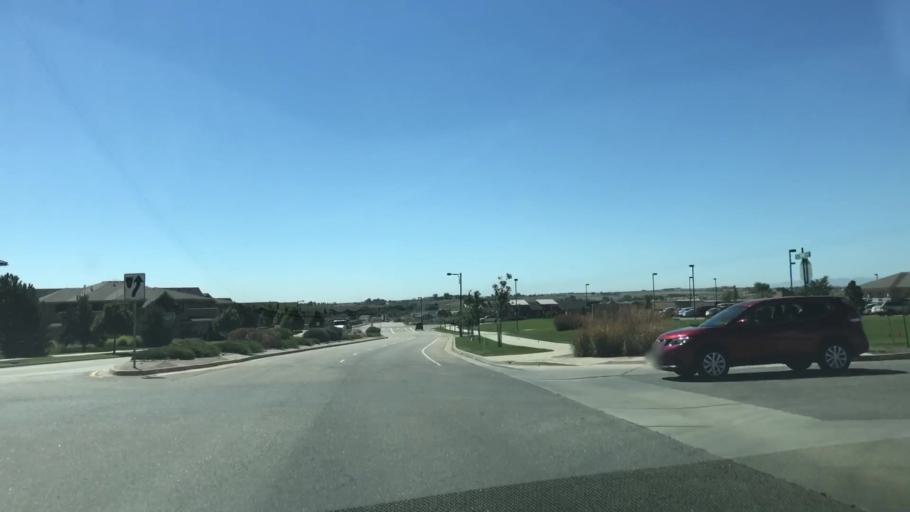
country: US
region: Colorado
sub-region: Weld County
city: Johnstown
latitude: 40.4055
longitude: -104.9739
